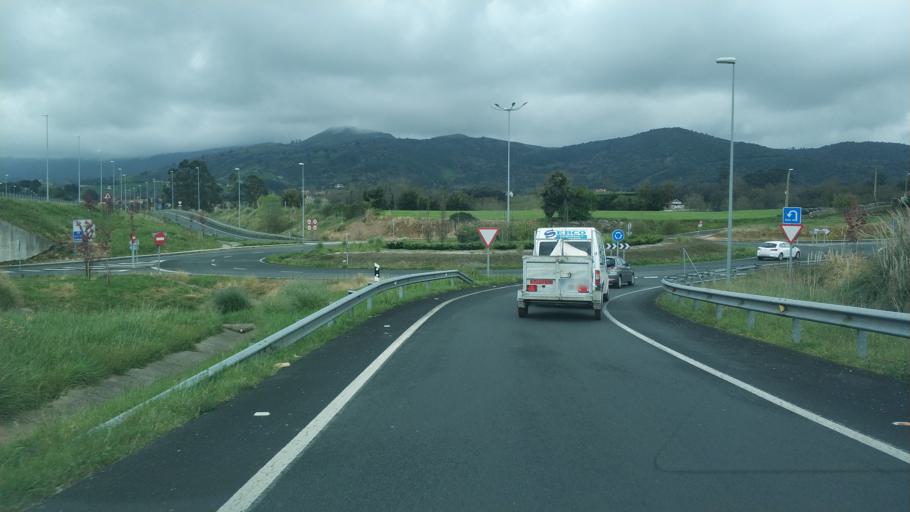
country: ES
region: Cantabria
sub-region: Provincia de Cantabria
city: Camargo
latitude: 43.3845
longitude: -3.8585
